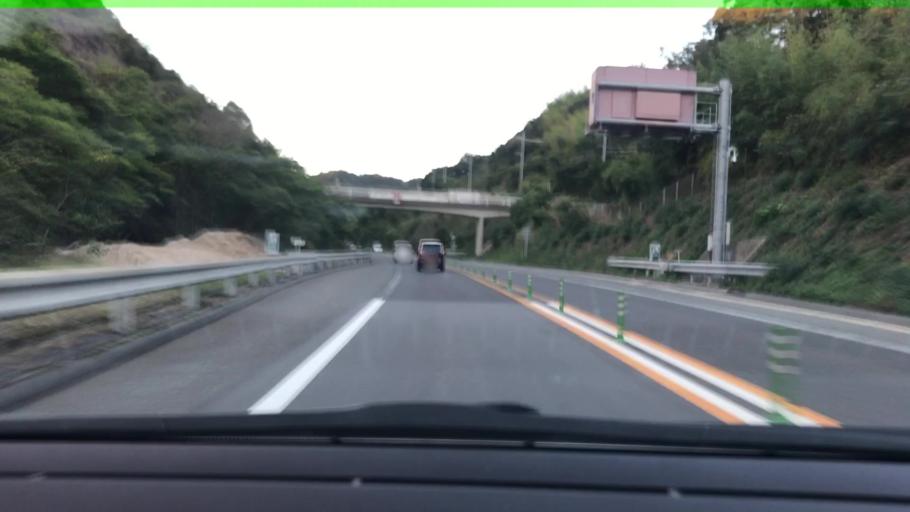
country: JP
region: Hiroshima
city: Innoshima
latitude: 34.3408
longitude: 133.1616
